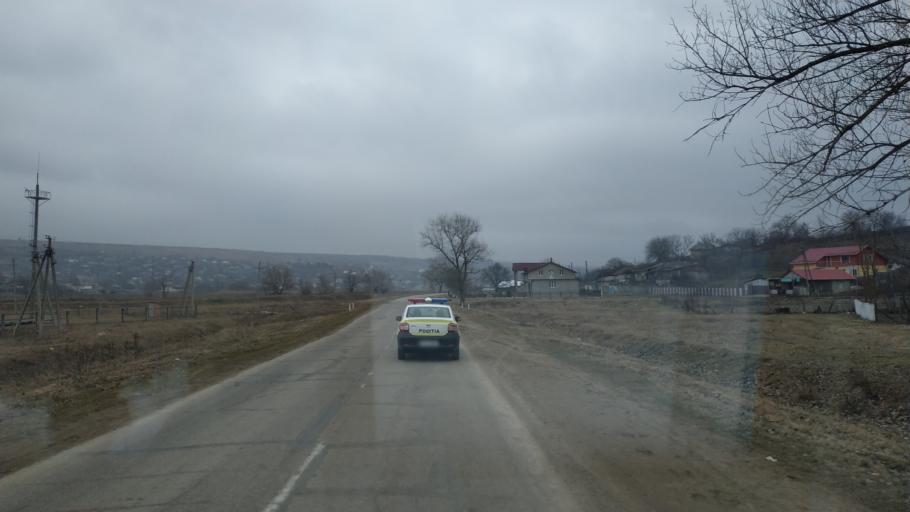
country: MD
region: Hincesti
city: Hincesti
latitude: 46.9770
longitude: 28.4650
